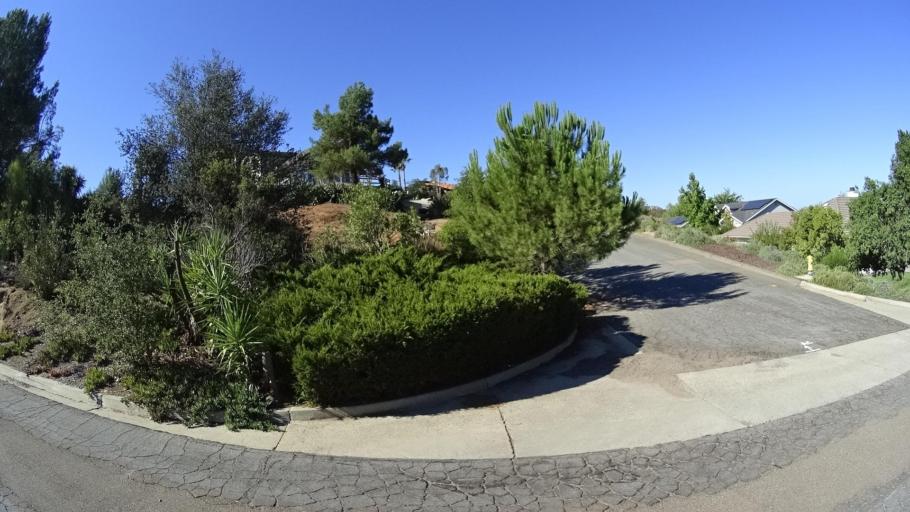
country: US
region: California
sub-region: San Diego County
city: San Diego Country Estates
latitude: 32.9983
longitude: -116.7570
